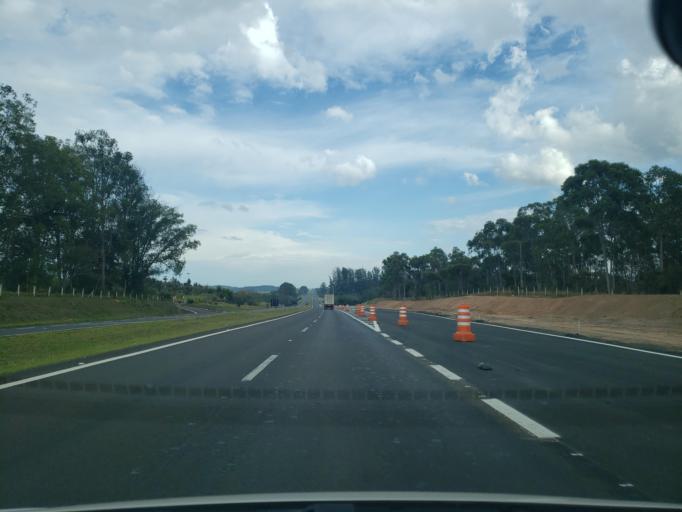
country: BR
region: Sao Paulo
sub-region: Itirapina
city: Itirapina
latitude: -22.2640
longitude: -47.9061
